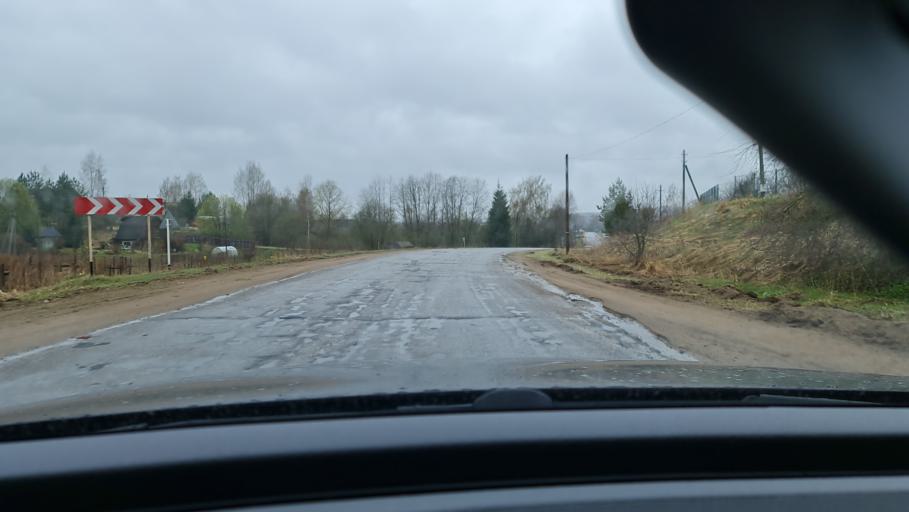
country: RU
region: Novgorod
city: Valday
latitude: 58.0317
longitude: 32.9714
